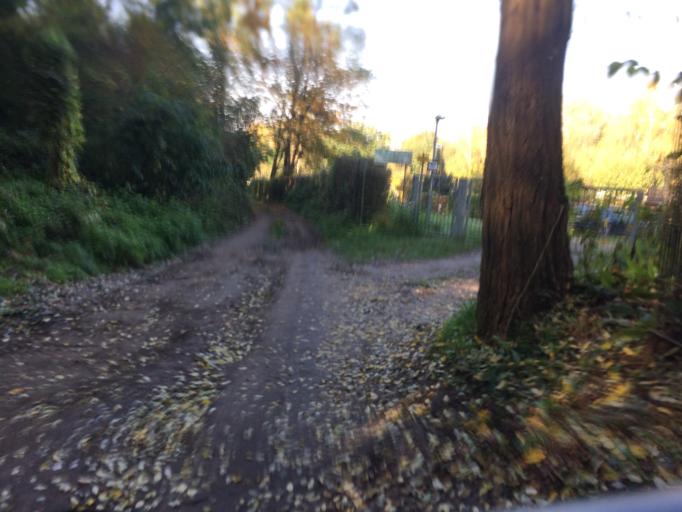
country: DE
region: Berlin
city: Blankenfelde
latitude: 52.6450
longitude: 13.3979
